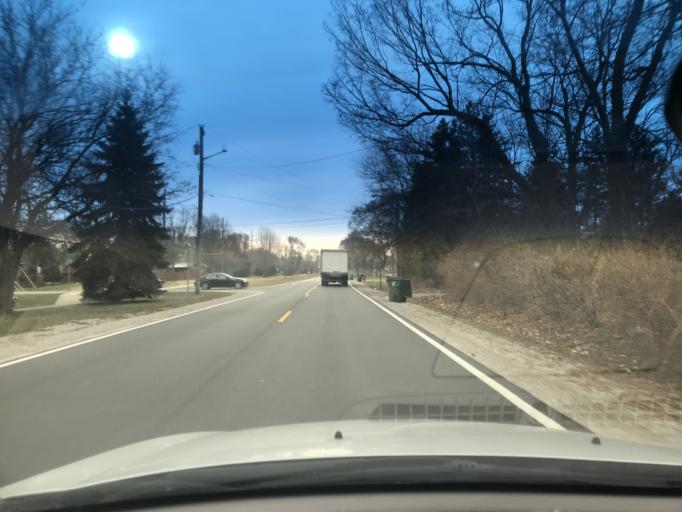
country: US
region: Michigan
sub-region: Macomb County
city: Shelby
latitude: 42.6805
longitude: -83.0540
